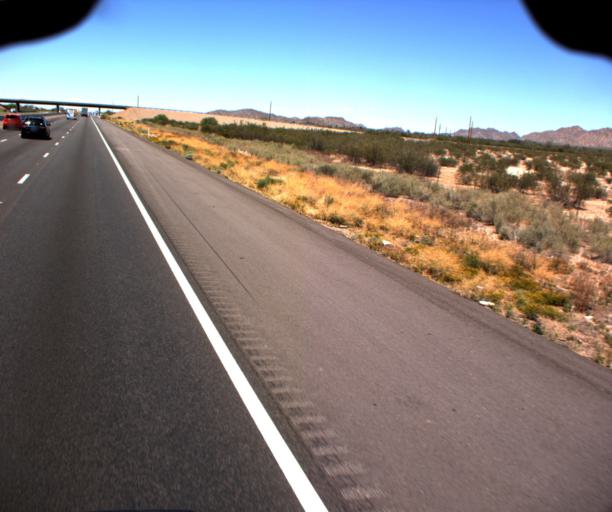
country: US
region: Arizona
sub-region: Pinal County
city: Casa Grande
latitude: 32.9646
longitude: -111.7218
